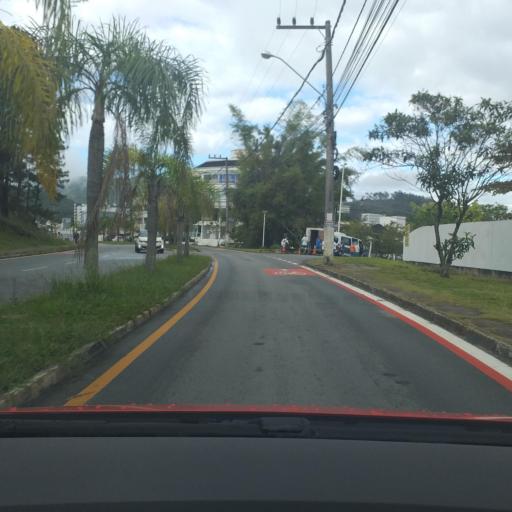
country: BR
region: Santa Catarina
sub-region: Florianopolis
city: Corrego Grande
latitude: -27.5964
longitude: -48.4988
